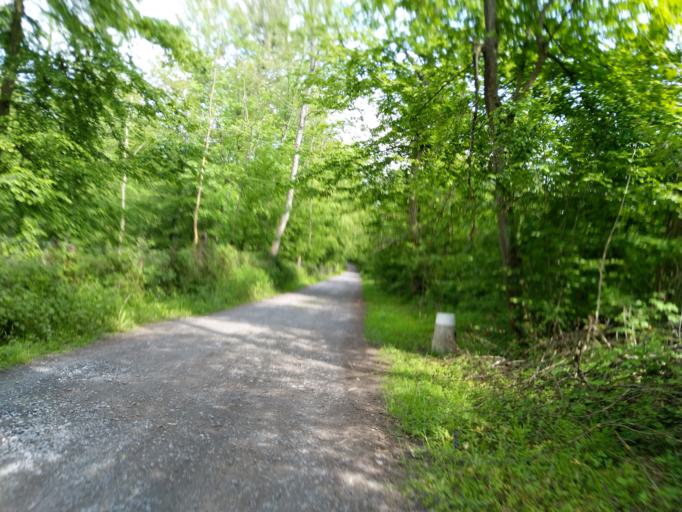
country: FR
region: Picardie
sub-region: Departement de l'Aisne
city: Boue
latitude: 50.0065
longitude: 3.7012
